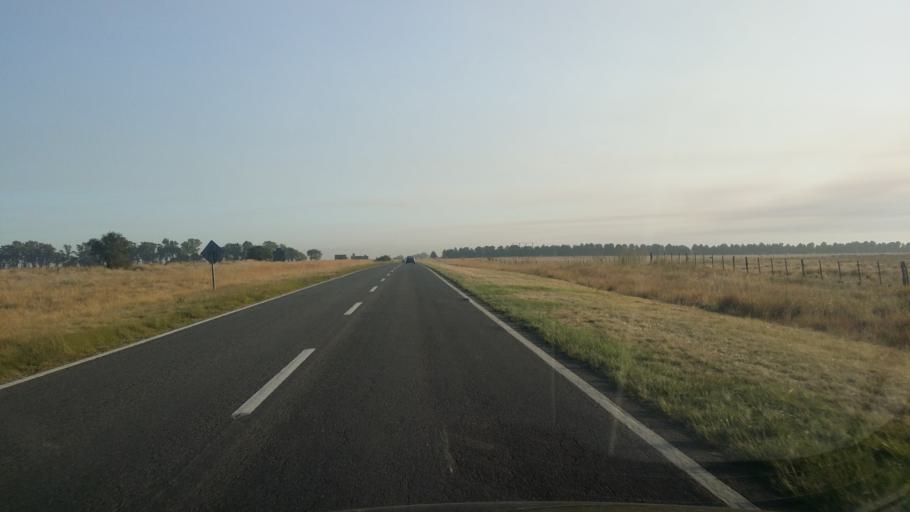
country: AR
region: La Pampa
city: Santa Rosa
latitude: -36.4721
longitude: -64.2798
